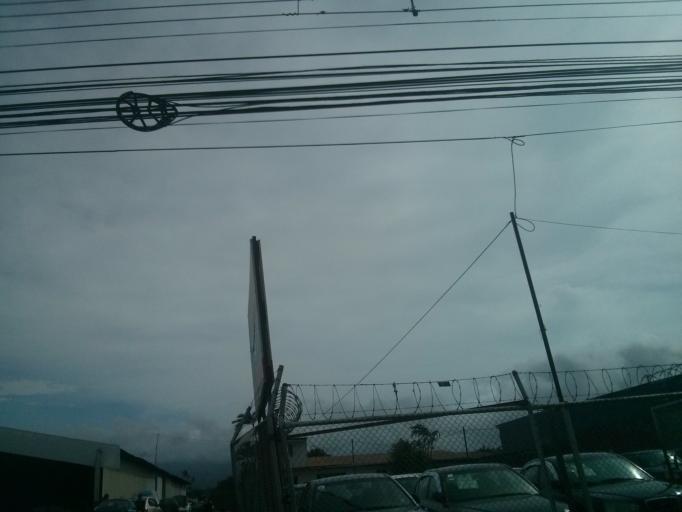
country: CR
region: San Jose
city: Colima
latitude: 9.9469
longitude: -84.0817
